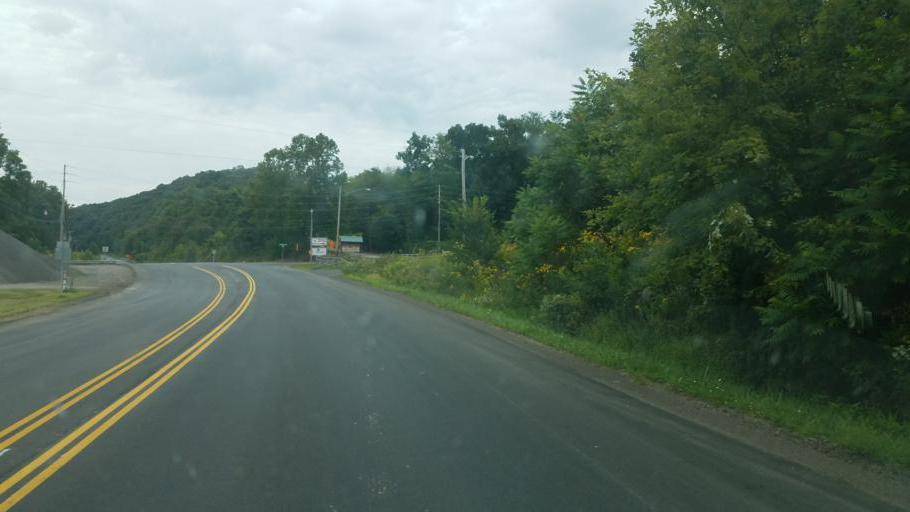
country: US
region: Ohio
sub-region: Columbiana County
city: Lisbon
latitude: 40.7649
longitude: -80.7117
